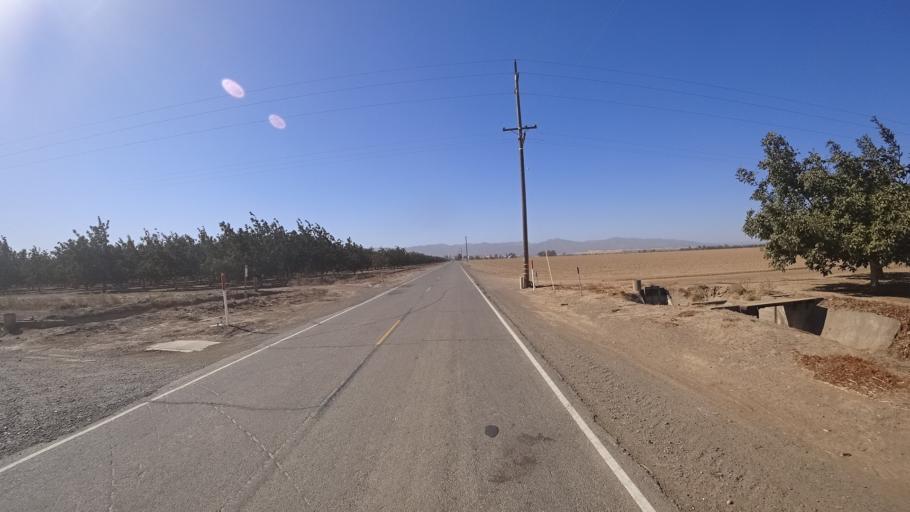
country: US
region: California
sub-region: Yolo County
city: Winters
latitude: 38.5839
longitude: -121.9619
